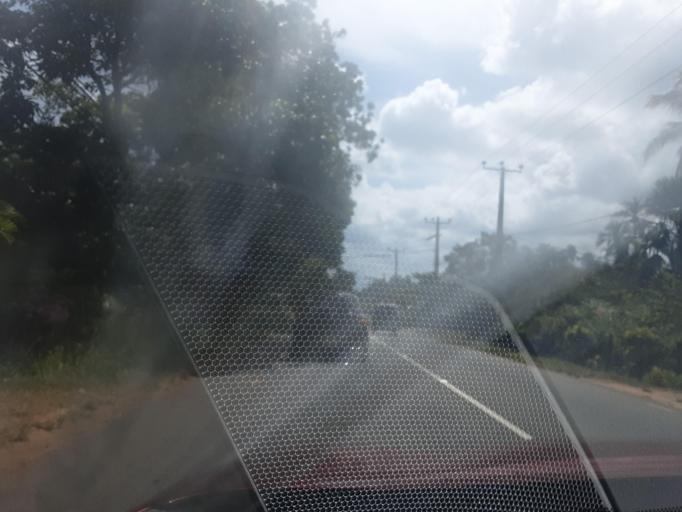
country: LK
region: North Western
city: Kuliyapitiya
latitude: 7.4842
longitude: 79.9760
